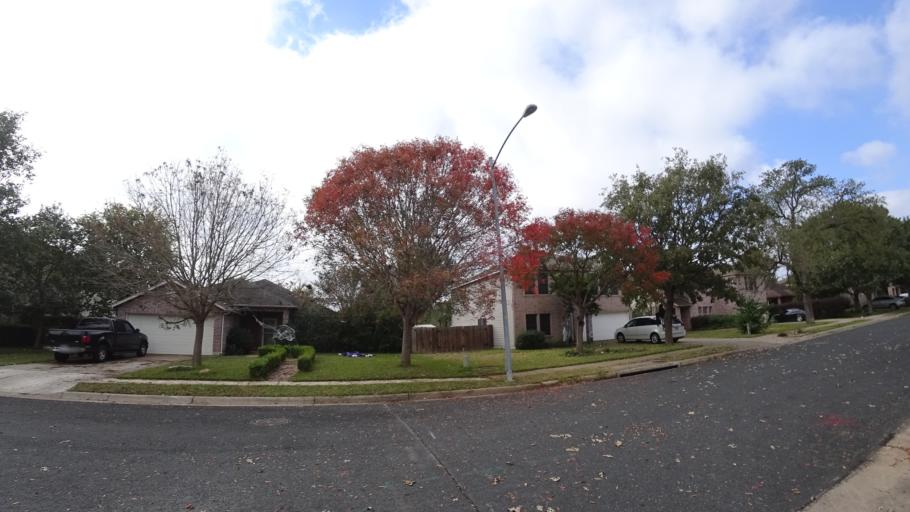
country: US
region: Texas
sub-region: Travis County
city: Shady Hollow
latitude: 30.2135
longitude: -97.8437
